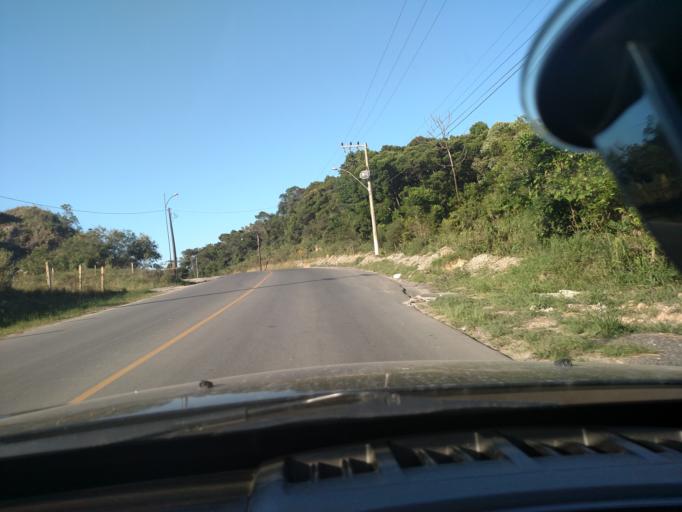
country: BR
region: Santa Catarina
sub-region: Porto Belo
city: Porto Belo
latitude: -27.1590
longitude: -48.5157
